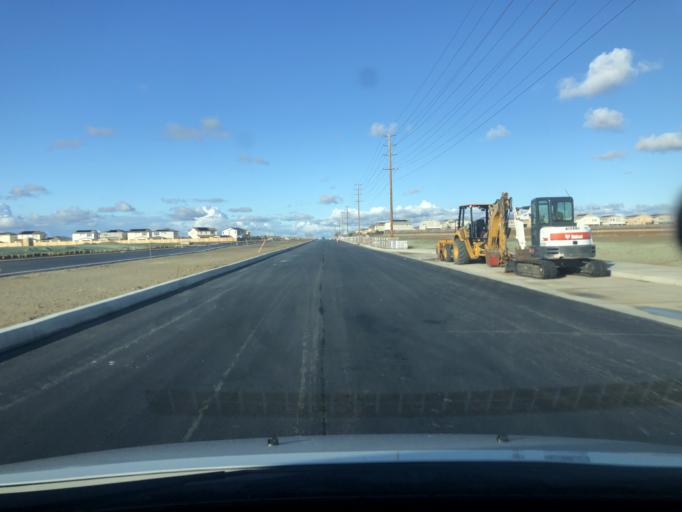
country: US
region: California
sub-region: Sacramento County
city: Antelope
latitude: 38.7667
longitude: -121.3852
